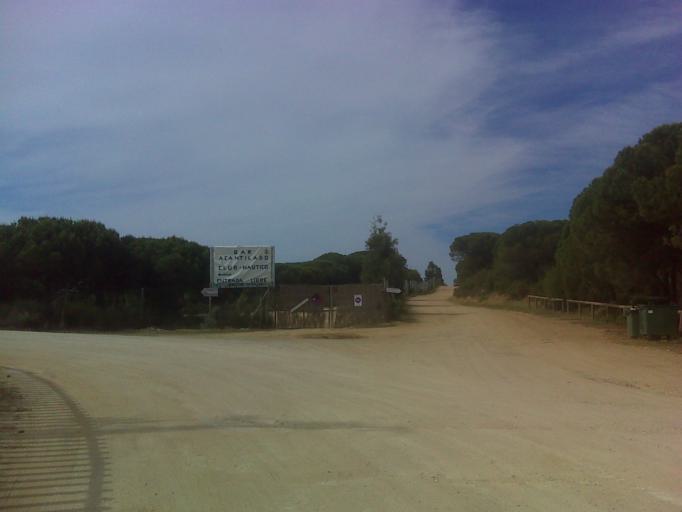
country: ES
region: Andalusia
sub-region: Provincia de Huelva
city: Mazagon
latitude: 37.0166
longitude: -6.5768
